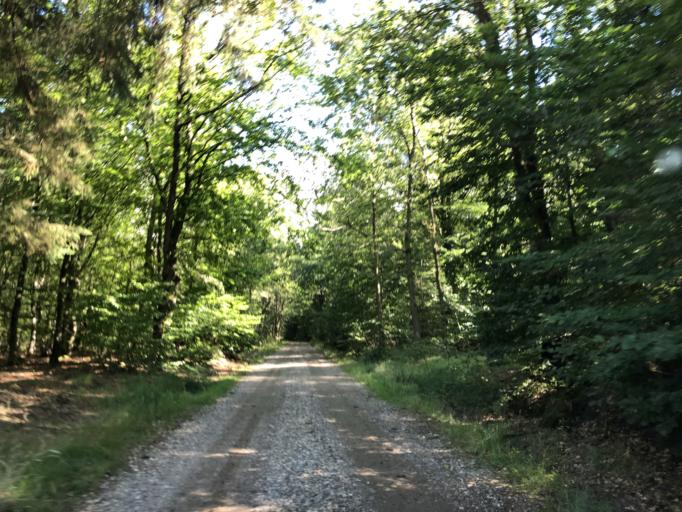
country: DK
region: Central Jutland
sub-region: Holstebro Kommune
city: Holstebro
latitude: 56.2451
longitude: 8.4930
